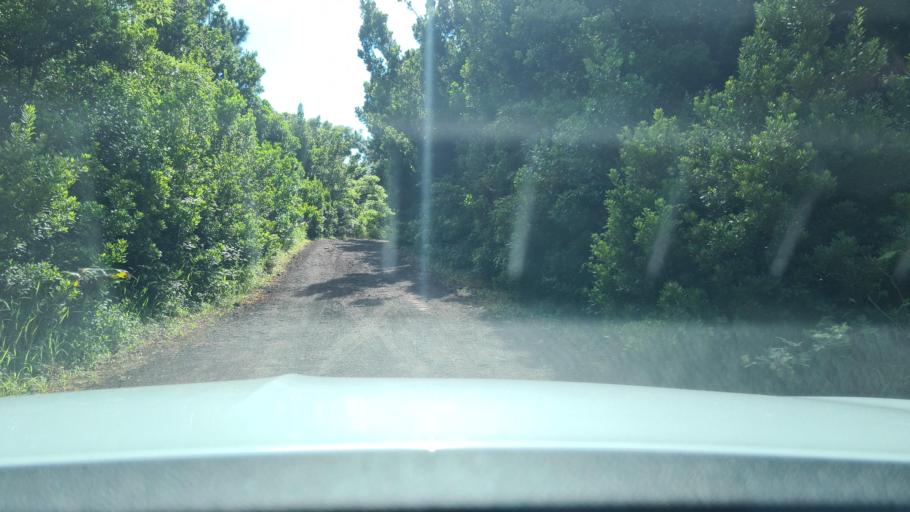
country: PT
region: Azores
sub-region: Sao Roque do Pico
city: Sao Roque do Pico
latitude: 38.4125
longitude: -28.3084
